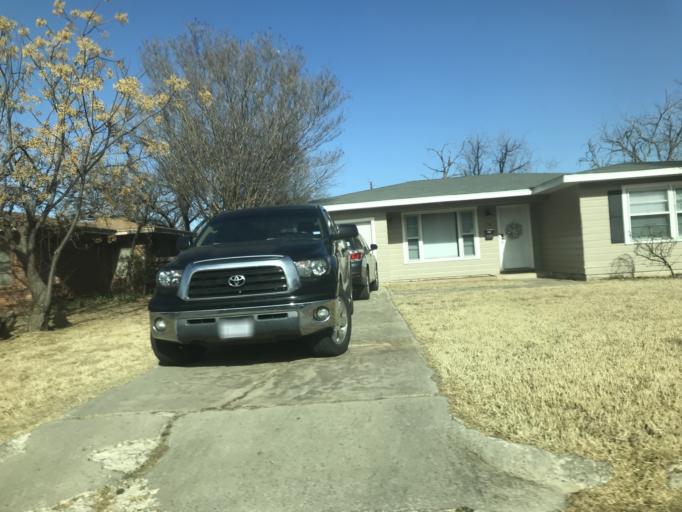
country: US
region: Texas
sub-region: Taylor County
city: Abilene
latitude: 32.4736
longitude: -99.7164
